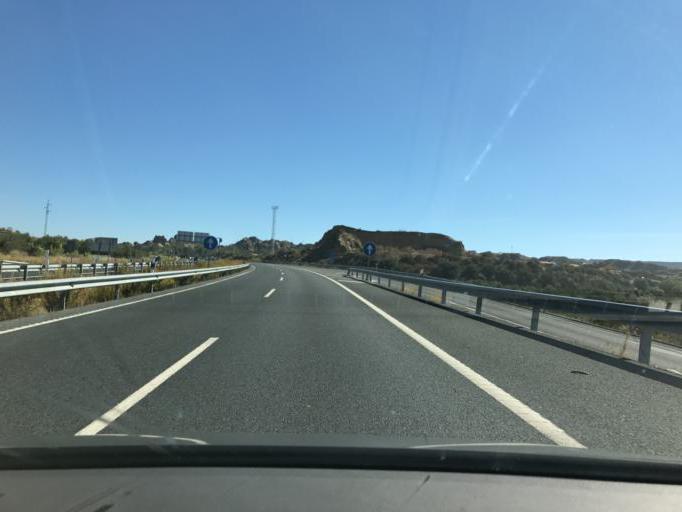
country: ES
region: Andalusia
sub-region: Provincia de Granada
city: Purullena
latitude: 37.3246
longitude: -3.2012
